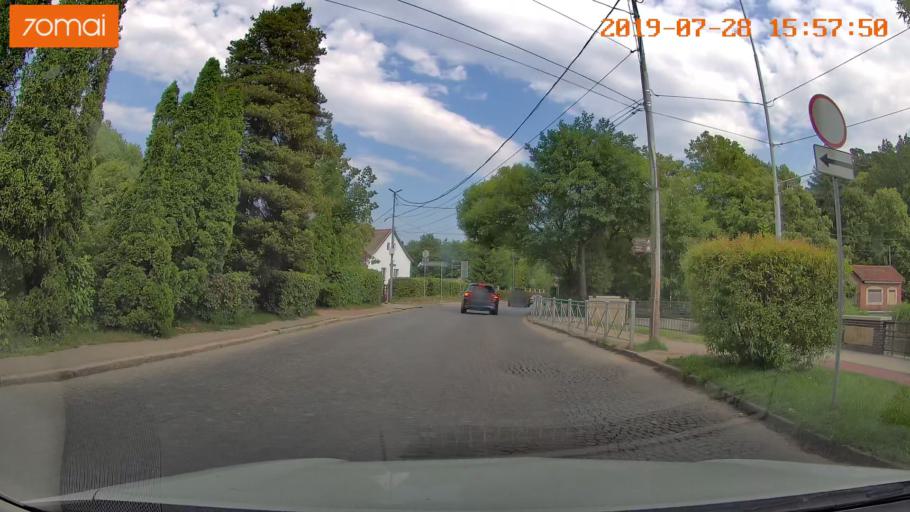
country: RU
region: Kaliningrad
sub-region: Gorod Svetlogorsk
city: Svetlogorsk
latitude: 54.9383
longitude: 20.1584
